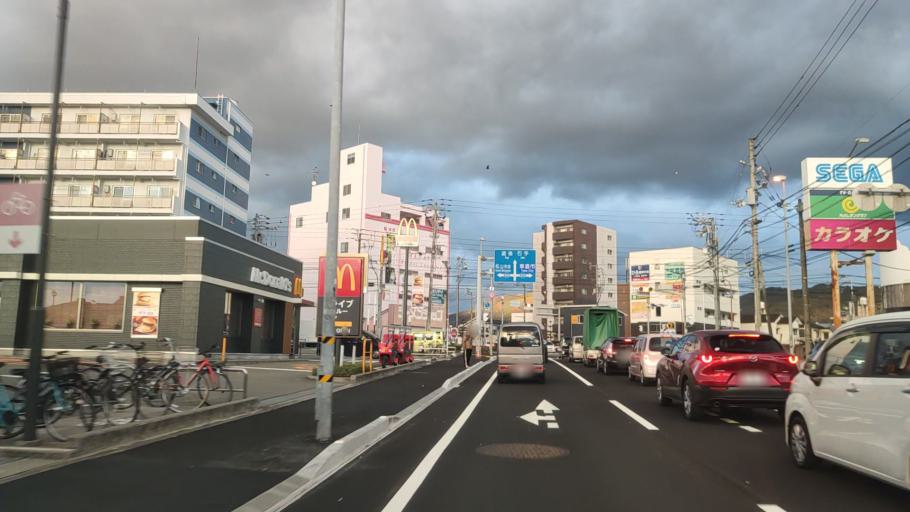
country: JP
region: Ehime
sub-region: Shikoku-chuo Shi
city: Matsuyama
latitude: 33.8285
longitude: 132.7861
